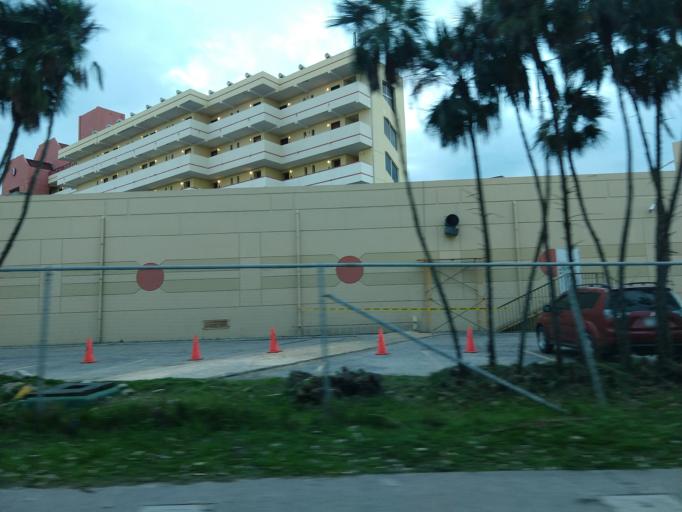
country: BZ
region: Belize
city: Belize City
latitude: 17.5043
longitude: -88.1885
